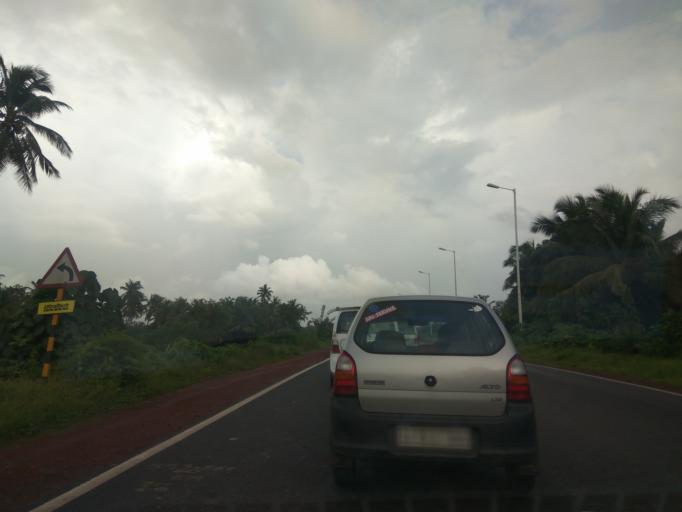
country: IN
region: Goa
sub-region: North Goa
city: Goa Velha
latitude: 15.4252
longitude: 73.8956
